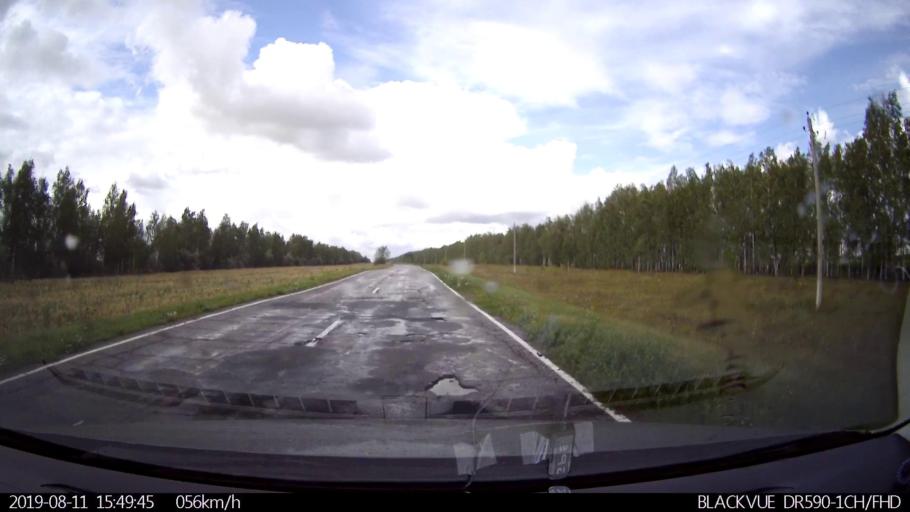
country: RU
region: Ulyanovsk
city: Ignatovka
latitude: 53.9069
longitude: 47.6554
